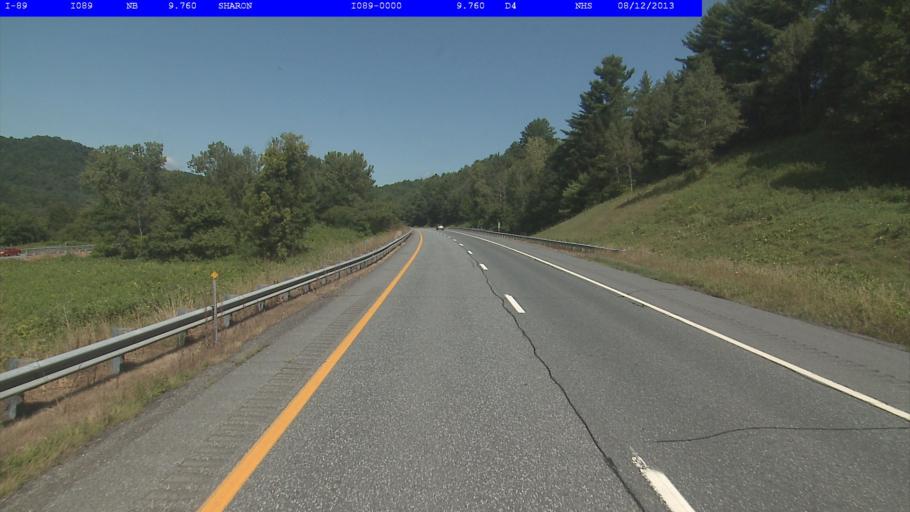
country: US
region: Vermont
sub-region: Windsor County
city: Wilder
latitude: 43.7387
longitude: -72.4336
